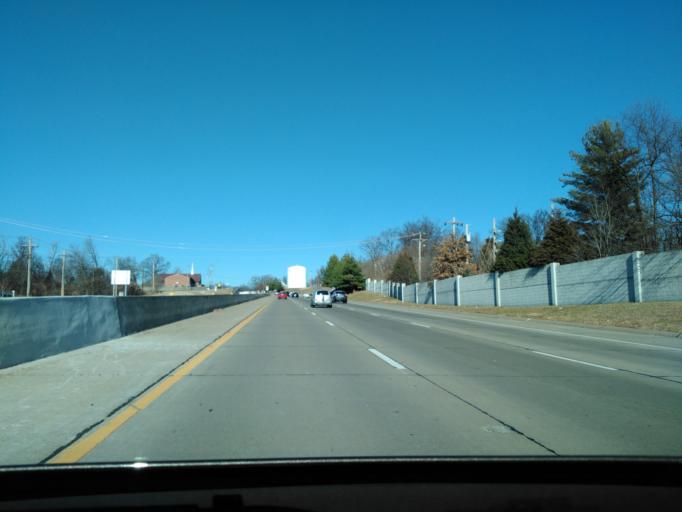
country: US
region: Missouri
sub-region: Saint Louis County
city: Valley Park
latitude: 38.5535
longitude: -90.4931
